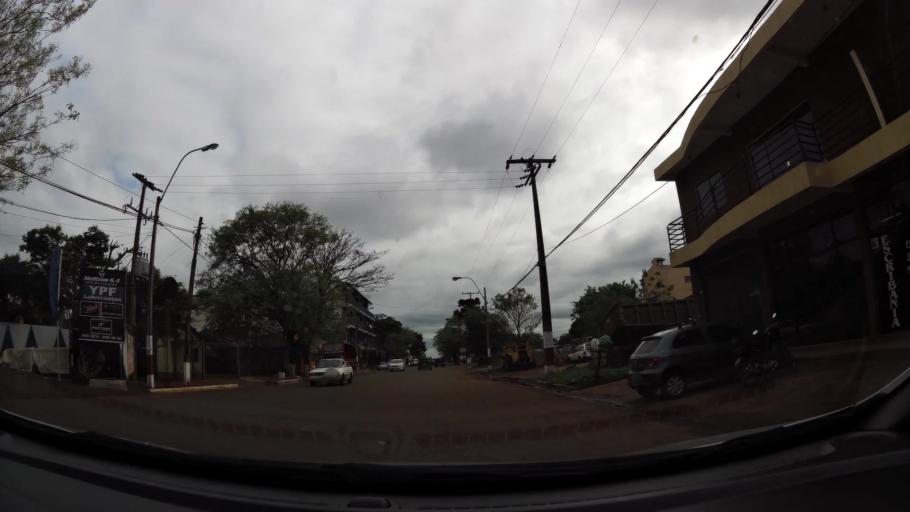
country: PY
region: Alto Parana
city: Ciudad del Este
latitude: -25.3943
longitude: -54.6374
